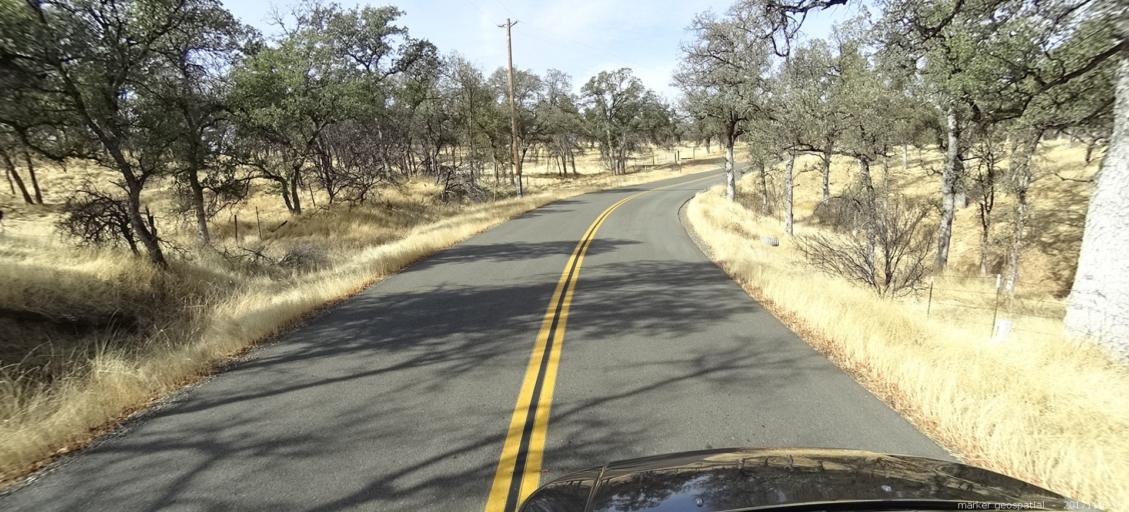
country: US
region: California
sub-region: Shasta County
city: Shasta
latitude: 40.4442
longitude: -122.5287
